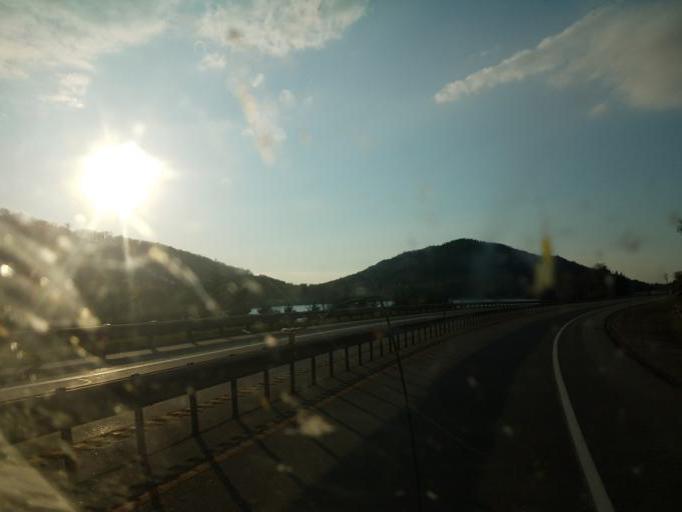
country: US
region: New Hampshire
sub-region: Grafton County
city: Deerfield
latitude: 44.1723
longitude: -71.6879
